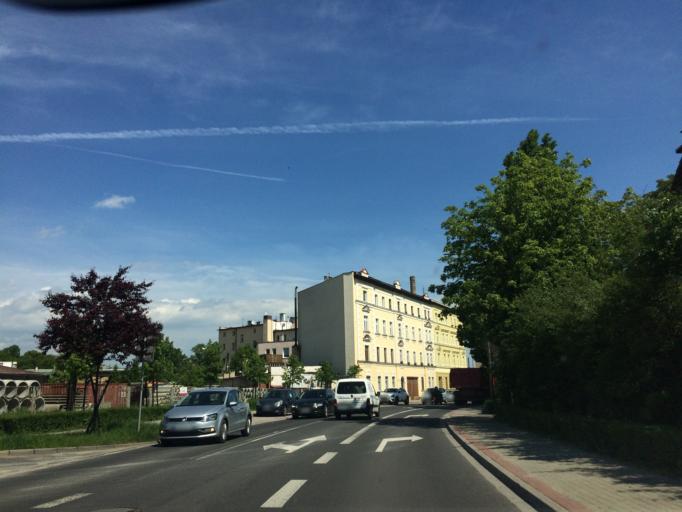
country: PL
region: Lower Silesian Voivodeship
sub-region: Powiat swidnicki
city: Swidnica
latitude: 50.8345
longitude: 16.4995
